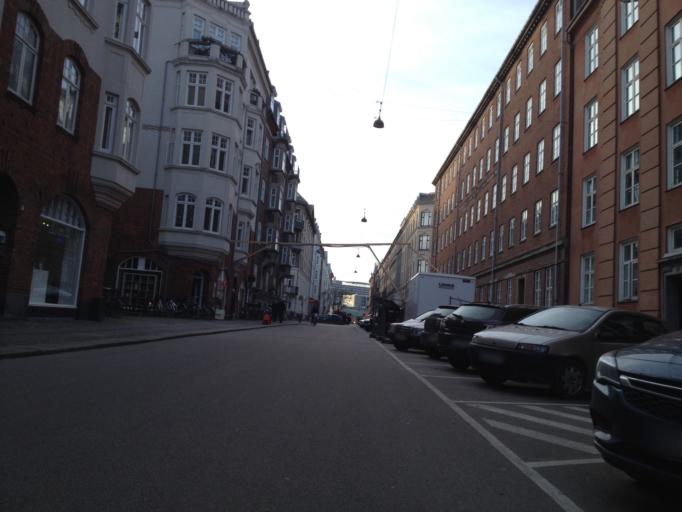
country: DK
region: Capital Region
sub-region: Kobenhavn
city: Copenhagen
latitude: 55.7004
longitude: 12.5819
